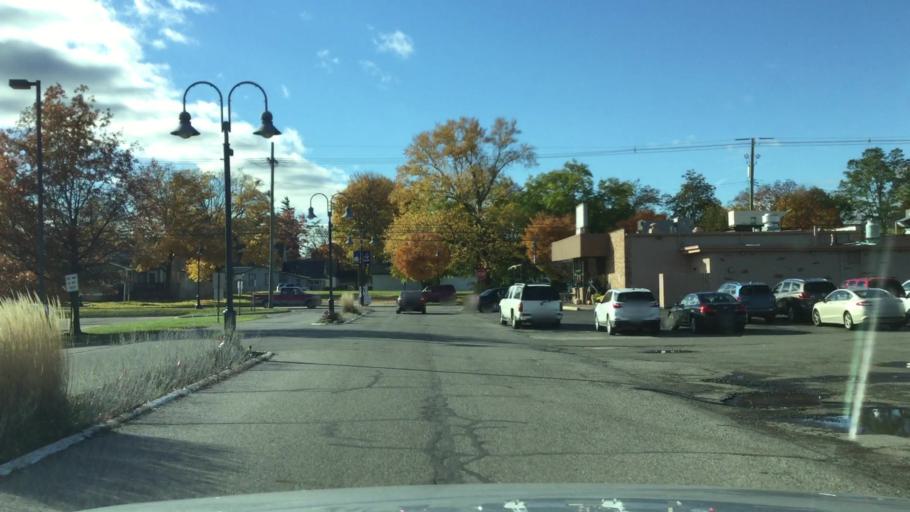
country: US
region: Michigan
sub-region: Oakland County
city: Keego Harbor
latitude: 42.6097
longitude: -83.3430
